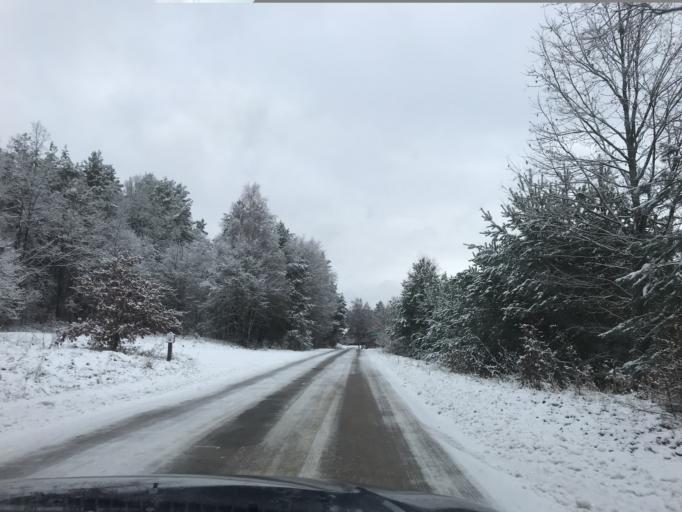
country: PL
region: Pomeranian Voivodeship
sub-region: Powiat bytowski
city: Parchowo
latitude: 54.2478
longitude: 17.5781
